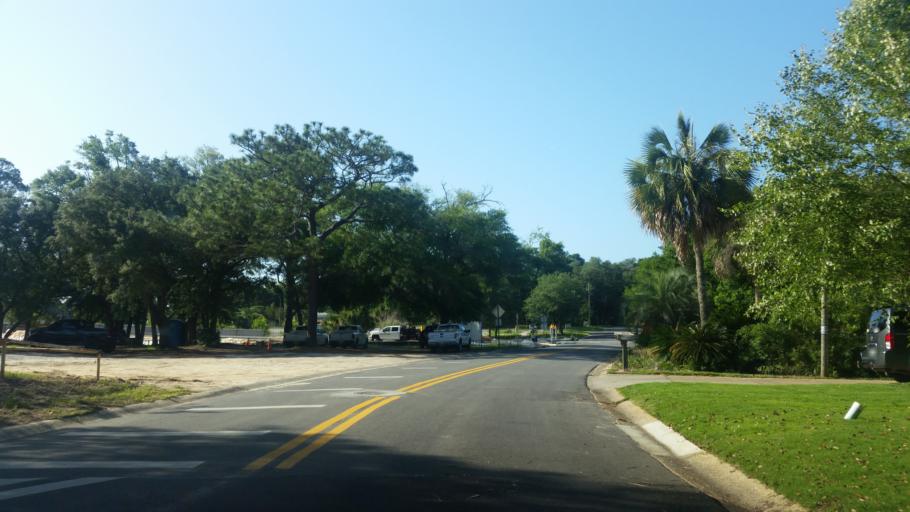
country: US
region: Florida
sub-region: Escambia County
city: Warrington
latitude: 30.3819
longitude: -87.2838
